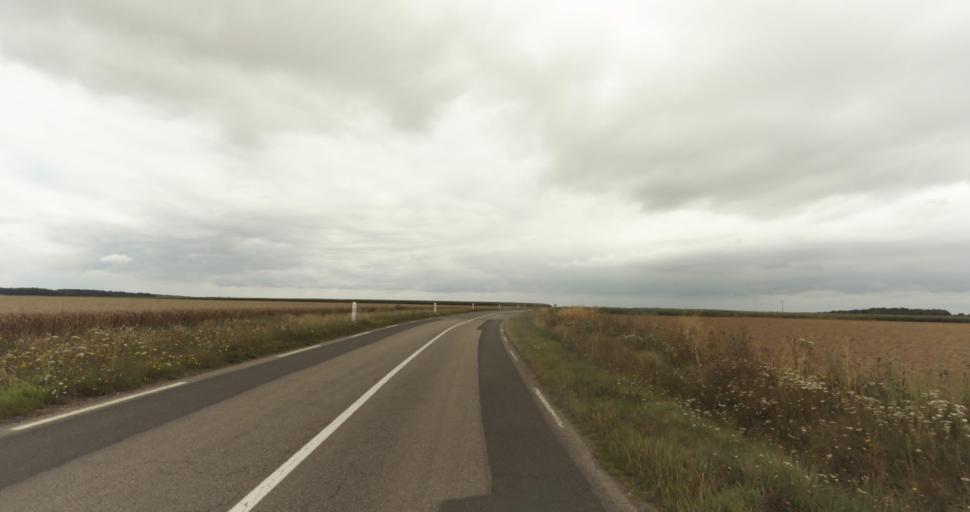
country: FR
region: Haute-Normandie
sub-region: Departement de l'Eure
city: Gravigny
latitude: 49.0508
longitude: 1.2279
